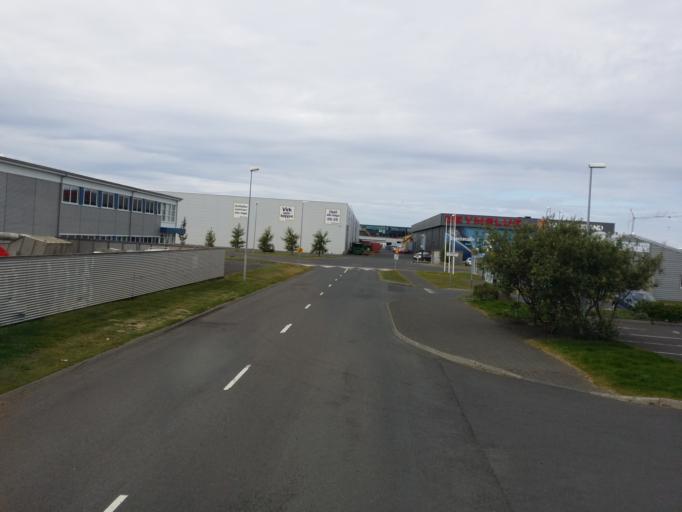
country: IS
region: Capital Region
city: Seltjarnarnes
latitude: 64.1543
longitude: -21.9475
